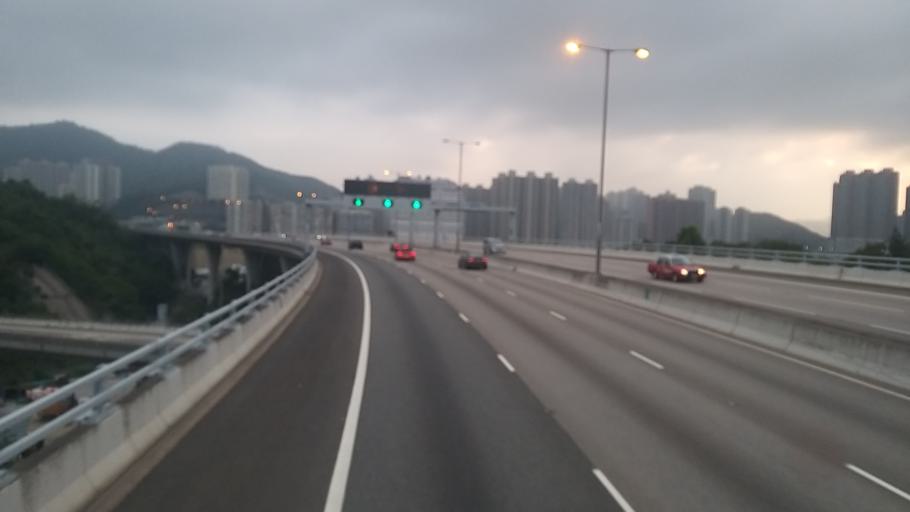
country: HK
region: Tsuen Wan
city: Tsuen Wan
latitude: 22.3523
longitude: 114.1198
